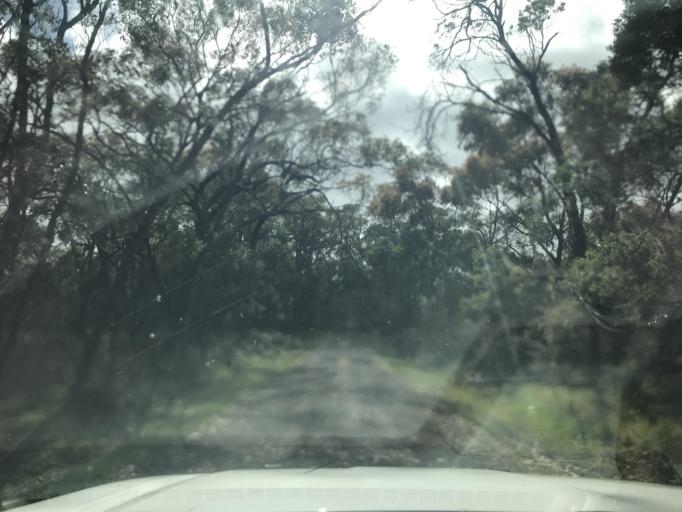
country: AU
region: South Australia
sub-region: Wattle Range
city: Penola
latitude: -37.3489
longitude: 141.3964
